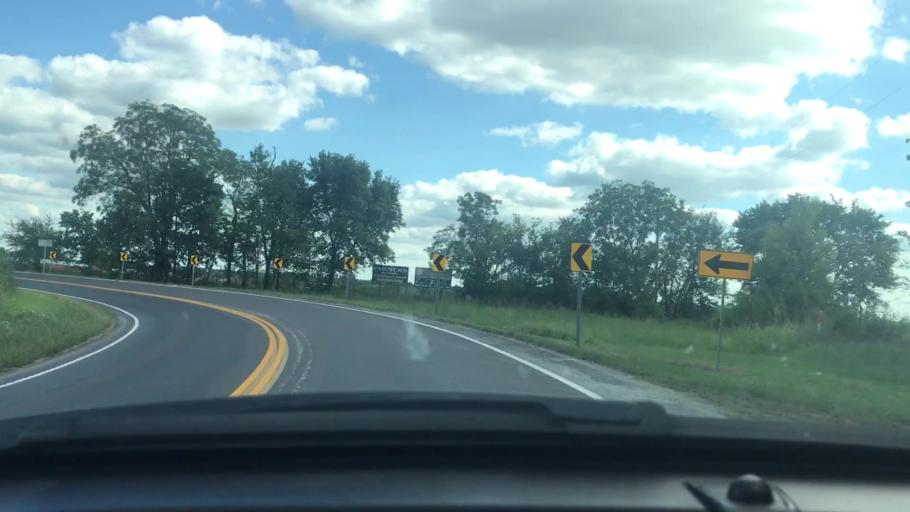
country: US
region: Missouri
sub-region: Wright County
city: Mountain Grove
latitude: 37.1660
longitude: -92.2672
